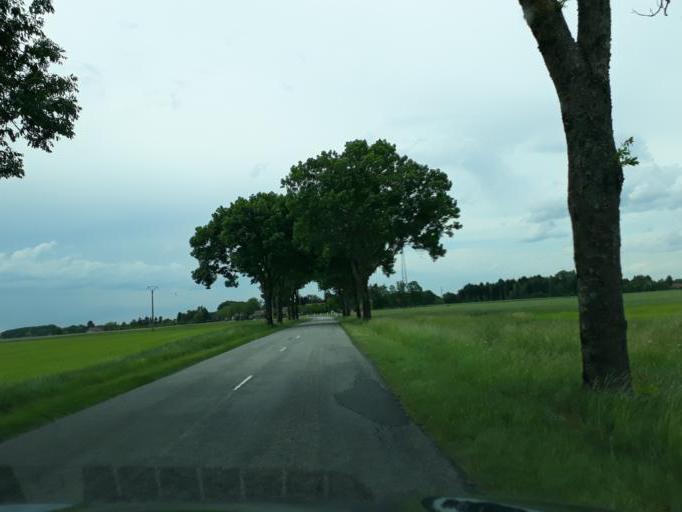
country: FR
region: Centre
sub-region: Departement du Loiret
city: Vienne-en-Val
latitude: 47.8316
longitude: 2.1449
